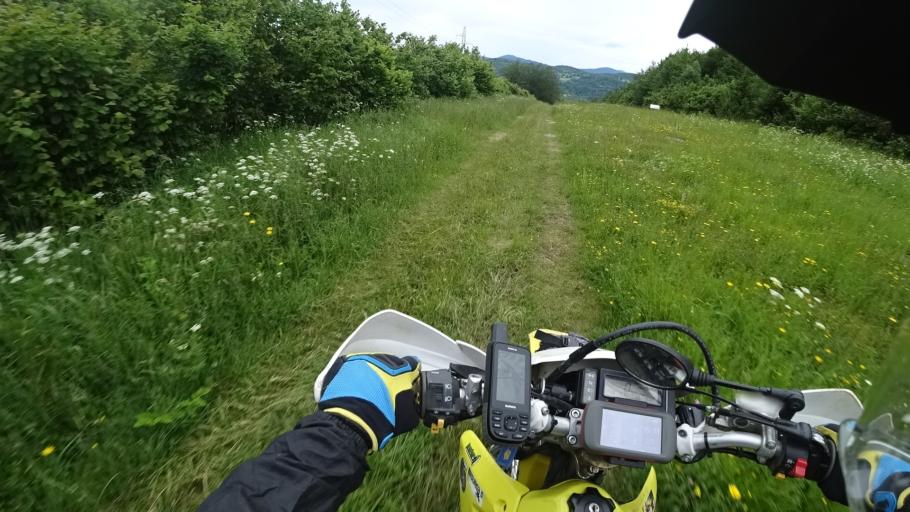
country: HR
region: Primorsko-Goranska
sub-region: Grad Delnice
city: Delnice
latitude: 45.3817
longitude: 14.8631
